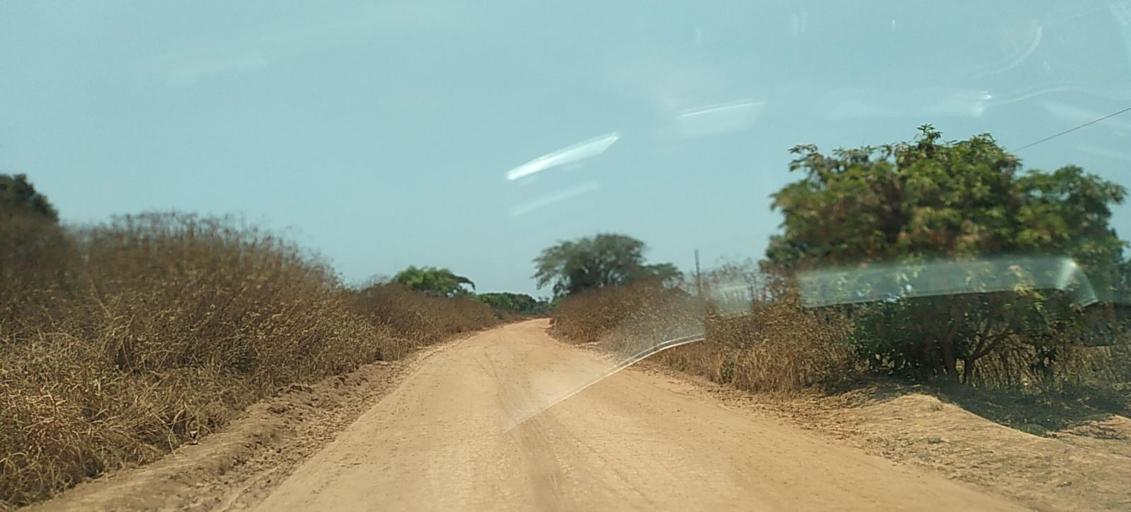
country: CD
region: Katanga
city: Kipushi
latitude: -11.7839
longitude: 27.1766
